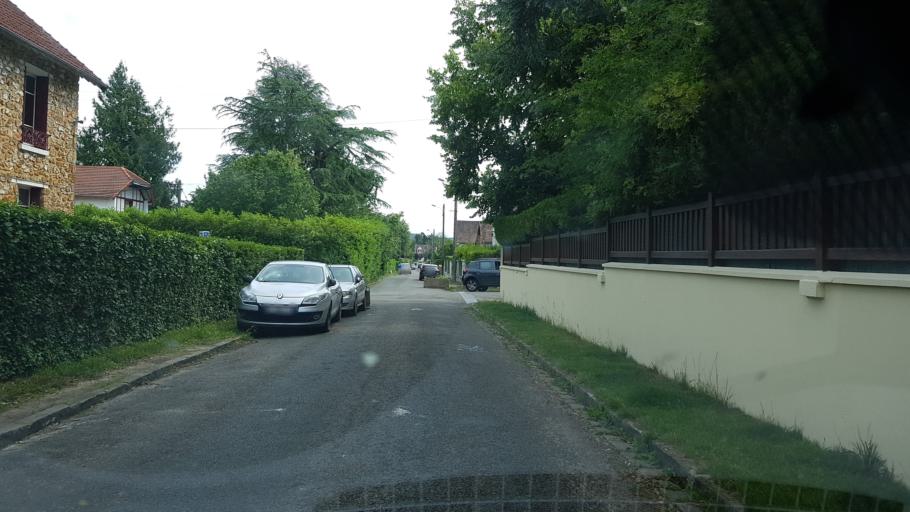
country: FR
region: Ile-de-France
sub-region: Departement des Yvelines
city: Saint-Remy-les-Chevreuse
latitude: 48.7142
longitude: 2.0658
